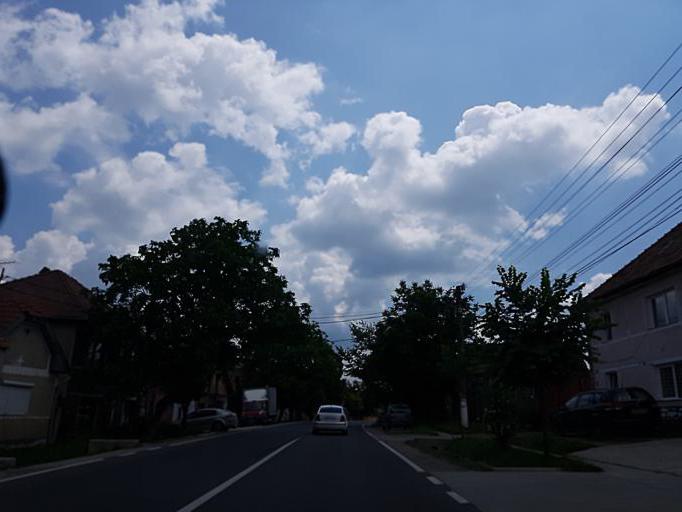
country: RO
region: Sibiu
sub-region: Comuna Slimnic
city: Slimnic
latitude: 45.9108
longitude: 24.1556
